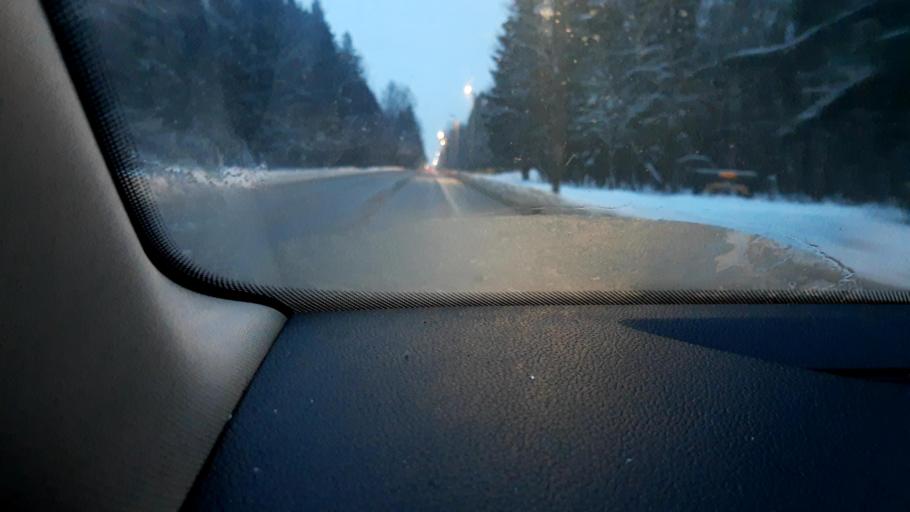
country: RU
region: Moskovskaya
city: Troitsk
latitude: 55.3139
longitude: 37.1626
